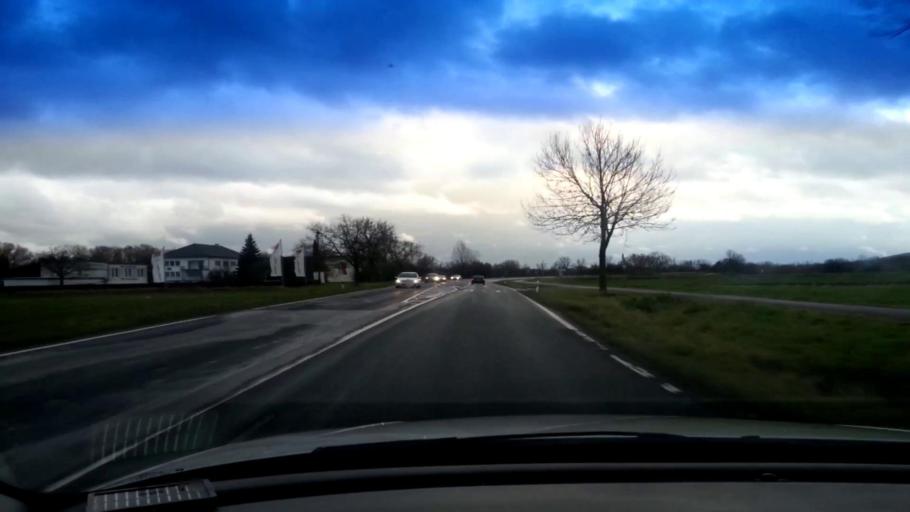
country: DE
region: Bavaria
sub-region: Upper Franconia
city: Breitengussbach
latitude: 49.9897
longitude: 10.8836
